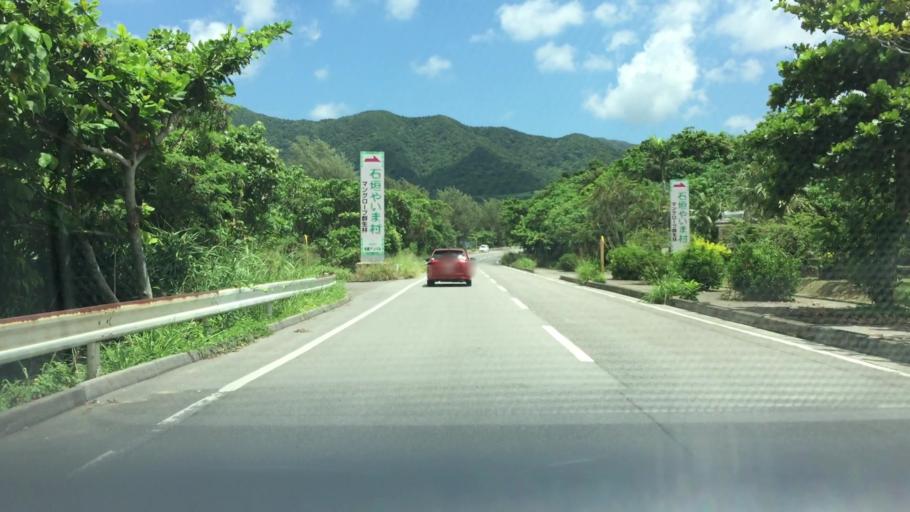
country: JP
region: Okinawa
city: Ishigaki
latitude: 24.4032
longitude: 124.1415
